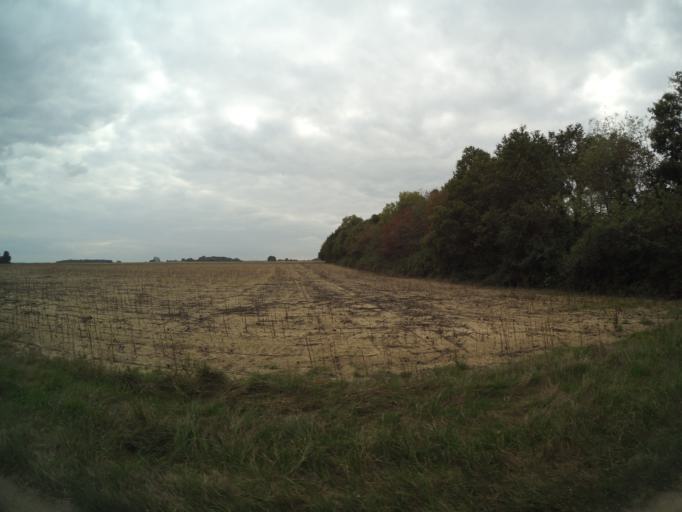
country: FR
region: Centre
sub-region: Departement d'Indre-et-Loire
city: Auzouer-en-Touraine
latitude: 47.5149
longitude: 0.9573
